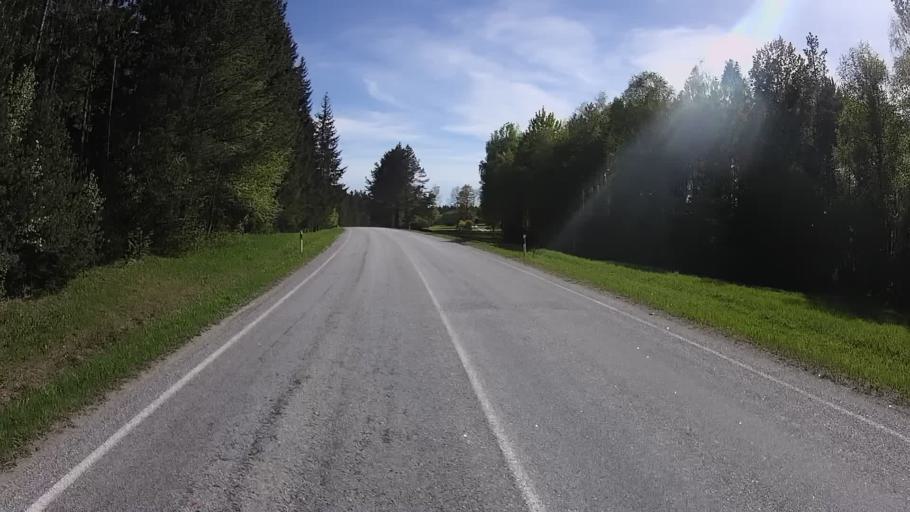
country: EE
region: Vorumaa
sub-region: Antsla vald
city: Vana-Antsla
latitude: 58.0150
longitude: 26.4984
